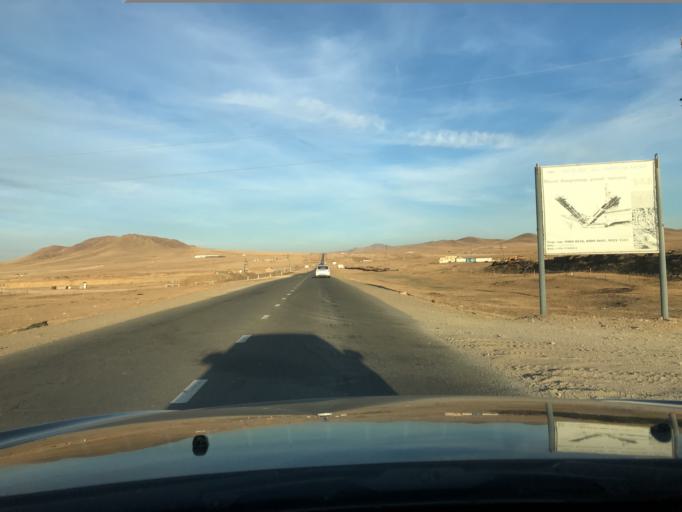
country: MN
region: Central Aimak
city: Arhust
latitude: 47.7890
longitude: 107.4735
